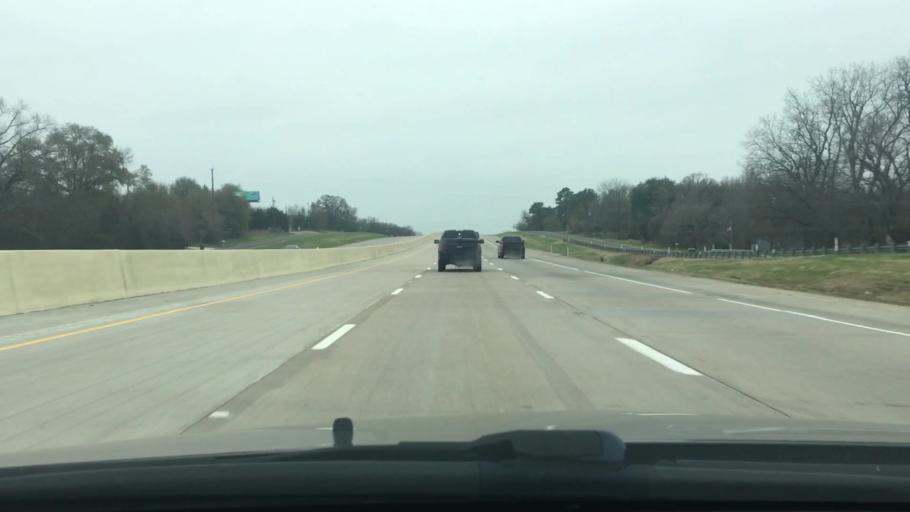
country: US
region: Texas
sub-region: Navarro County
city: Corsicana
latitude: 31.9619
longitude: -96.4205
